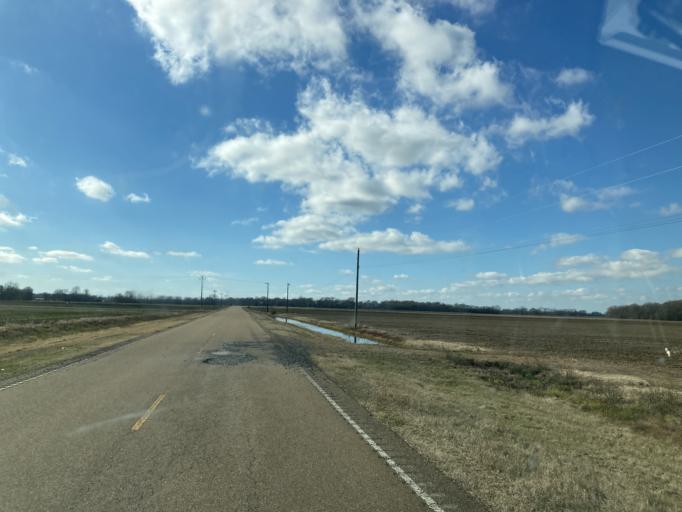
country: US
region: Mississippi
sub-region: Yazoo County
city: Yazoo City
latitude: 32.9625
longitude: -90.4868
